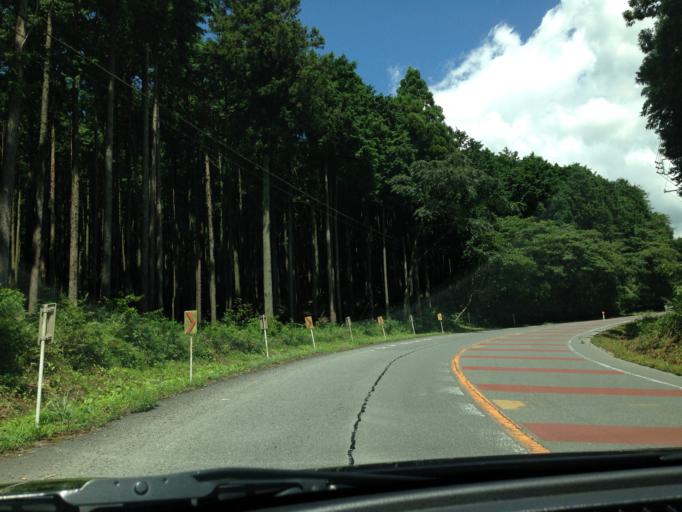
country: JP
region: Shizuoka
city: Fuji
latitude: 35.2165
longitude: 138.7304
